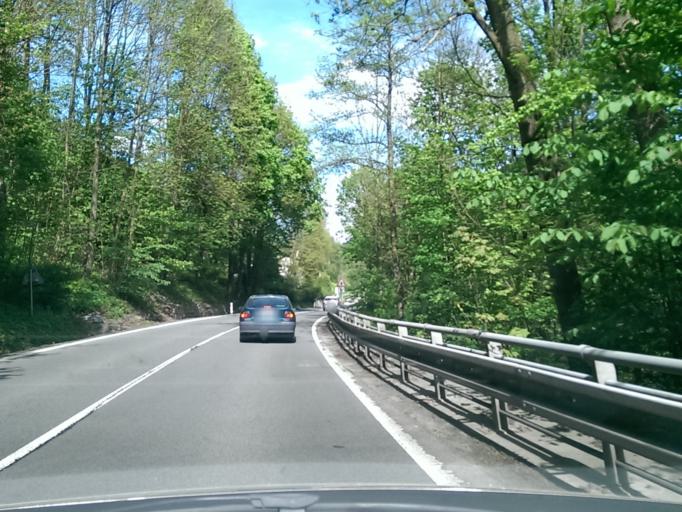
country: CZ
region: Liberecky
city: Mala Skala
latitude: 50.6261
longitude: 15.1795
